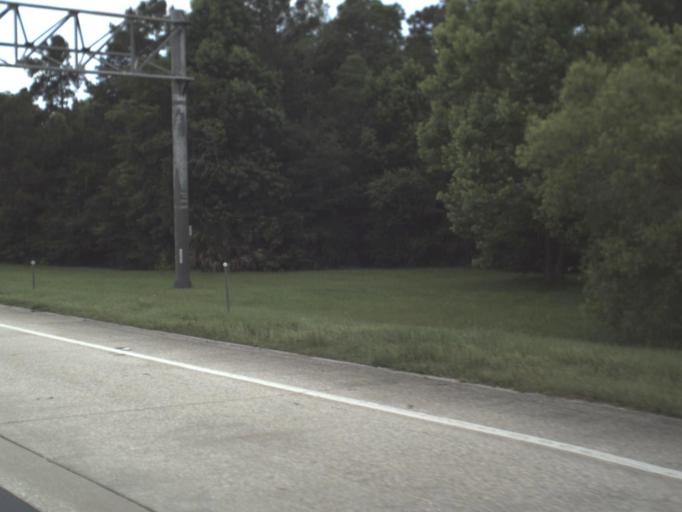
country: US
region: Florida
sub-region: Saint Johns County
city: Fruit Cove
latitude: 30.1692
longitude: -81.5351
